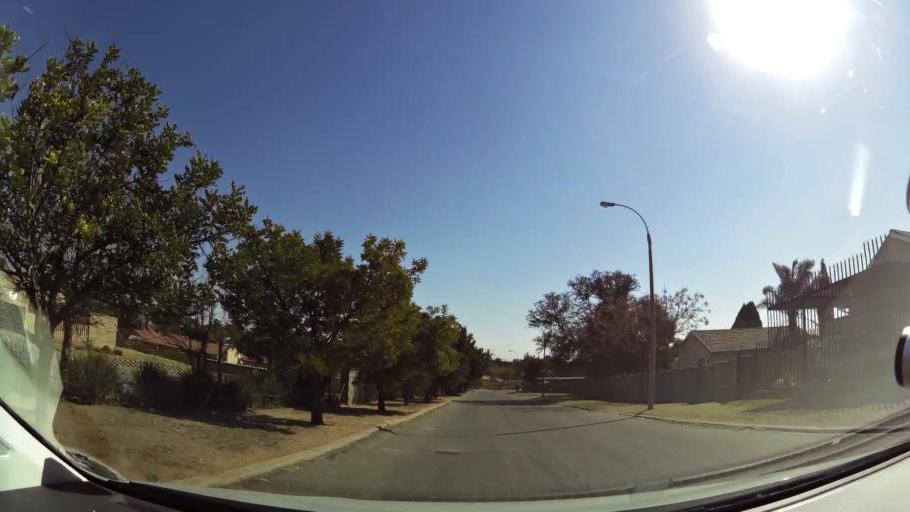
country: ZA
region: Gauteng
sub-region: Ekurhuleni Metropolitan Municipality
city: Tembisa
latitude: -26.0515
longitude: 28.2231
